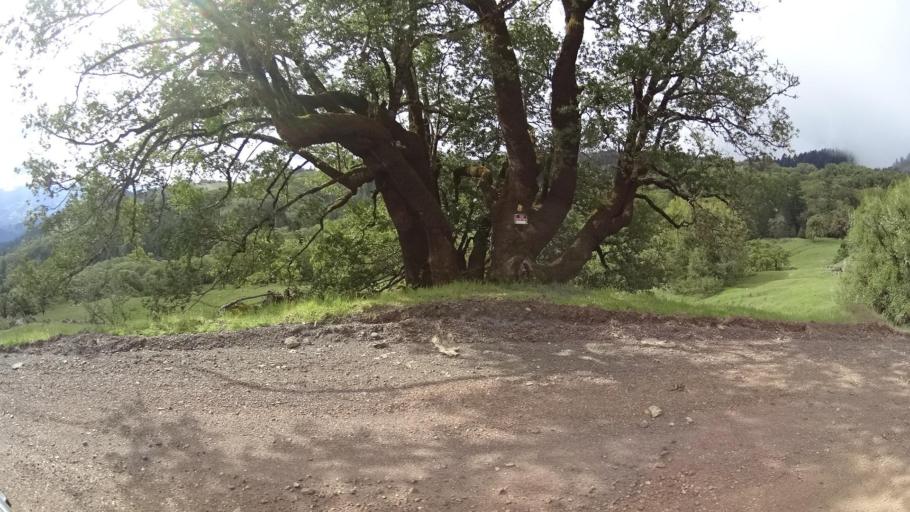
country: US
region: California
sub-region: Humboldt County
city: Redway
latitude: 40.1998
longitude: -123.6948
